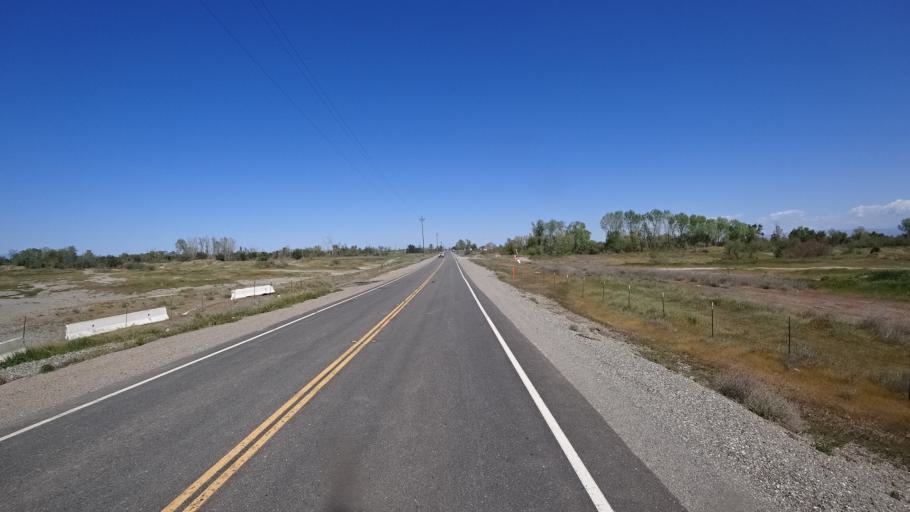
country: US
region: California
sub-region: Glenn County
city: Orland
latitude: 39.7602
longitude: -122.1409
